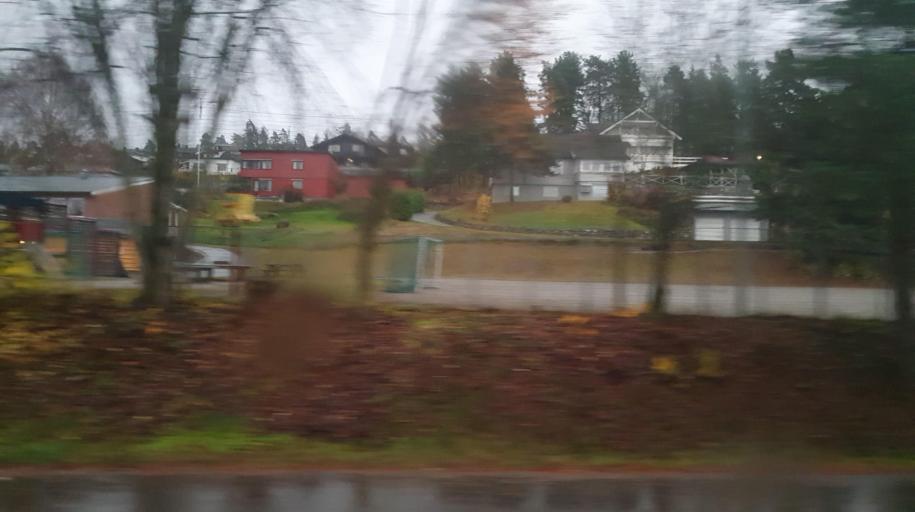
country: NO
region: Buskerud
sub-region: Modum
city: Vikersund
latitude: 59.8913
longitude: 9.9260
